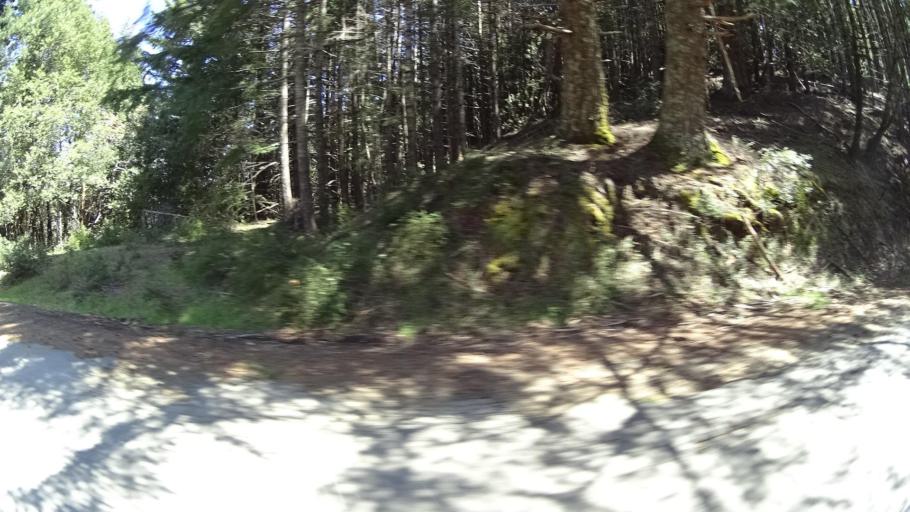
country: US
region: California
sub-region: Humboldt County
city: Rio Dell
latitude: 40.2891
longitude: -124.0562
